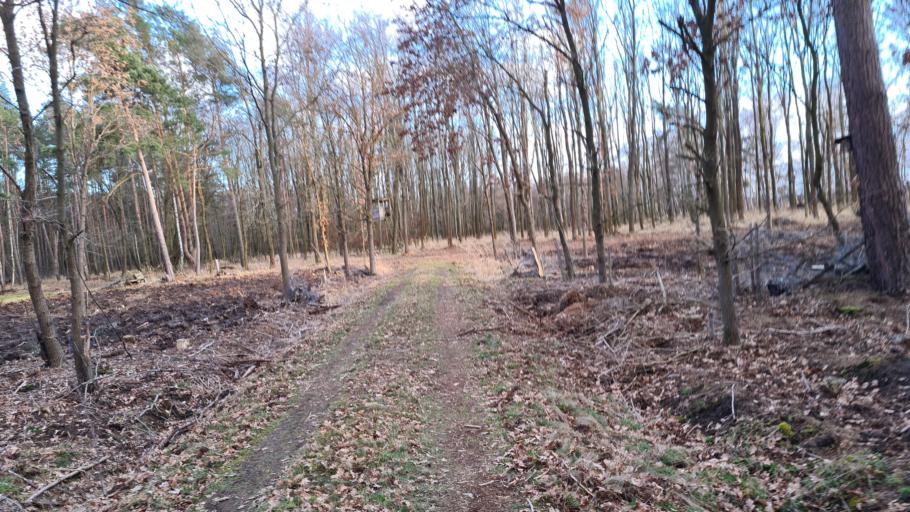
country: DE
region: Brandenburg
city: Schilda
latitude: 51.5751
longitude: 13.3159
